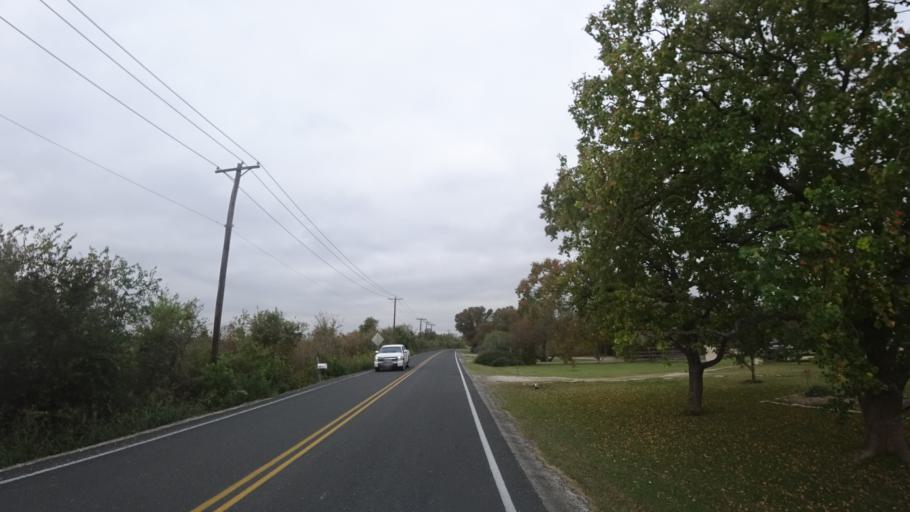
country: US
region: Texas
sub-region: Travis County
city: Pflugerville
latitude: 30.3950
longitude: -97.5971
